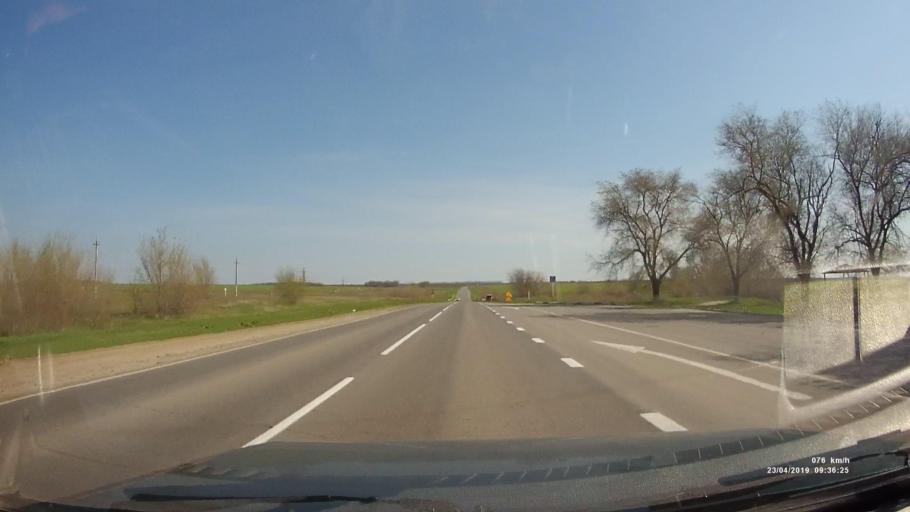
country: RU
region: Rostov
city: Gundorovskiy
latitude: 46.8325
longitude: 41.8807
